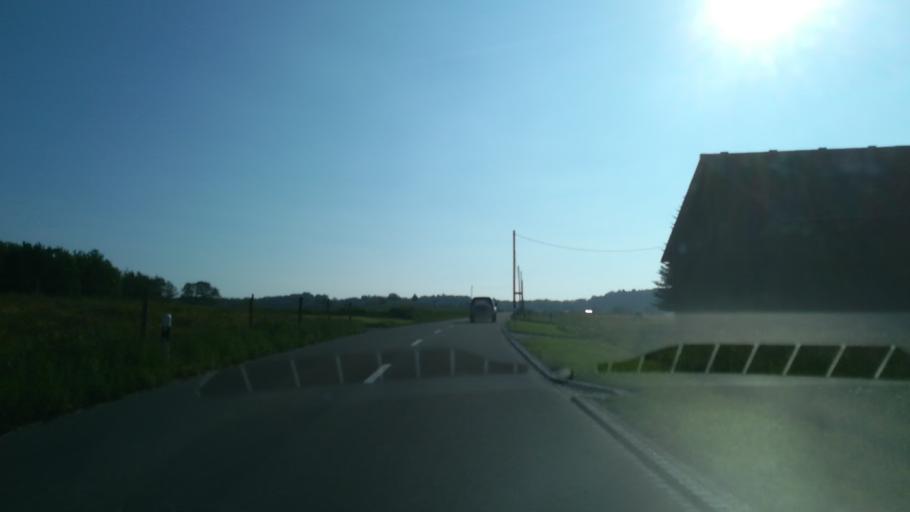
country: CH
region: Thurgau
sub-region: Kreuzlingen District
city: Ermatingen
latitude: 47.6388
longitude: 9.0586
